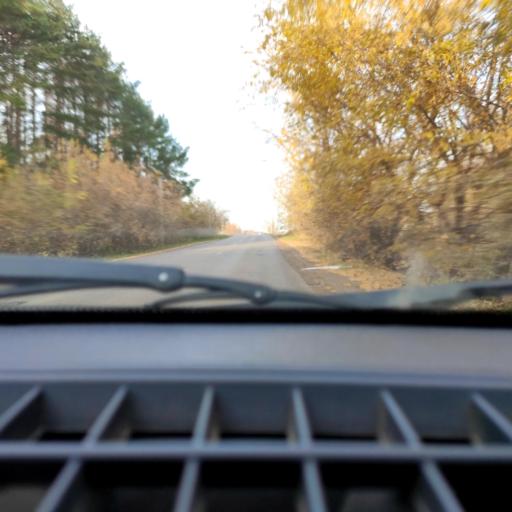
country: RU
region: Bashkortostan
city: Avdon
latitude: 54.6565
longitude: 55.7537
